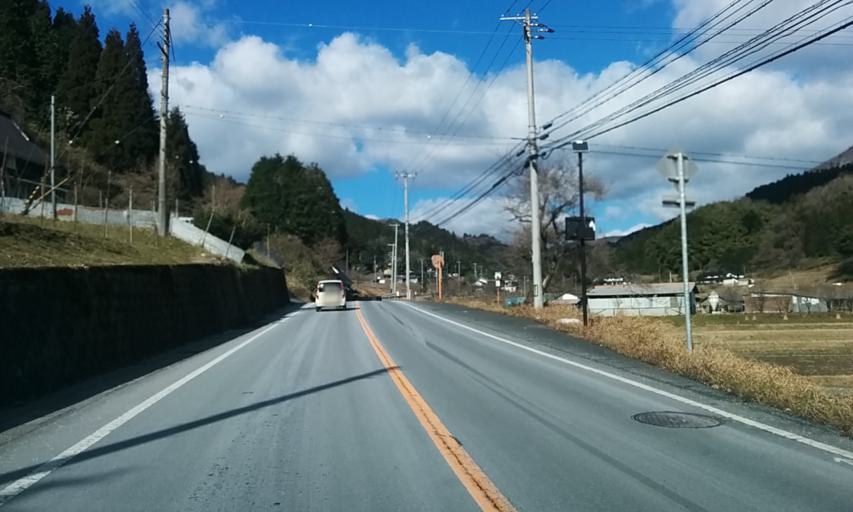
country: JP
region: Kyoto
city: Fukuchiyama
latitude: 35.3707
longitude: 135.0467
